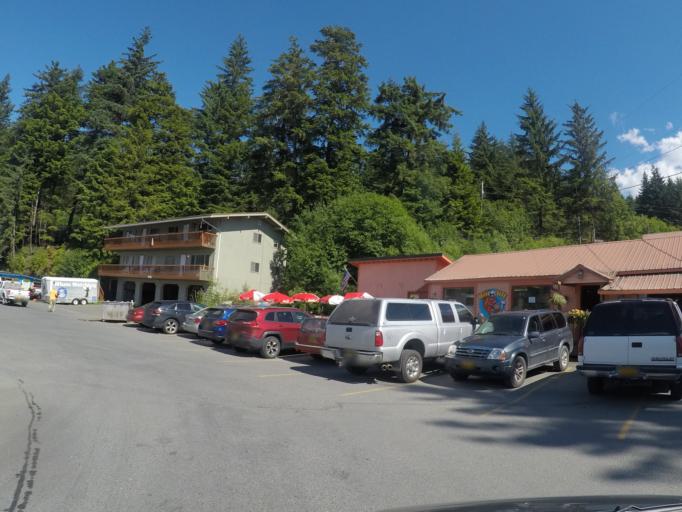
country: US
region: Alaska
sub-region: Juneau City and Borough
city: Juneau
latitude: 58.3841
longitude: -134.6457
